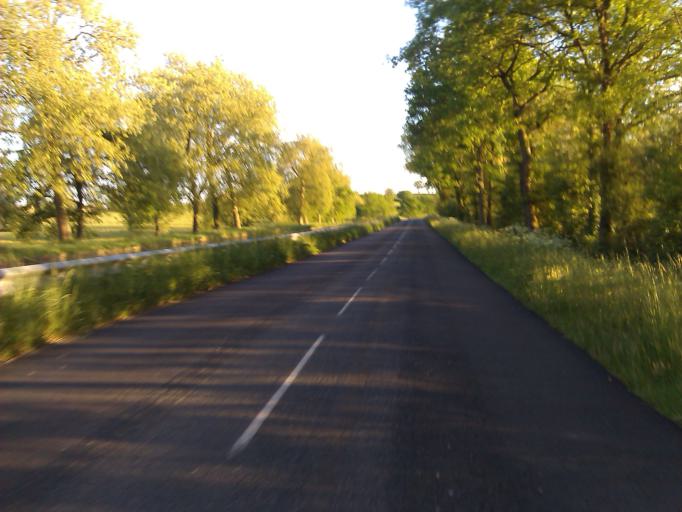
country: FR
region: Bourgogne
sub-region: Departement de Saone-et-Loire
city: Palinges
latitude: 46.5122
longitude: 4.1942
